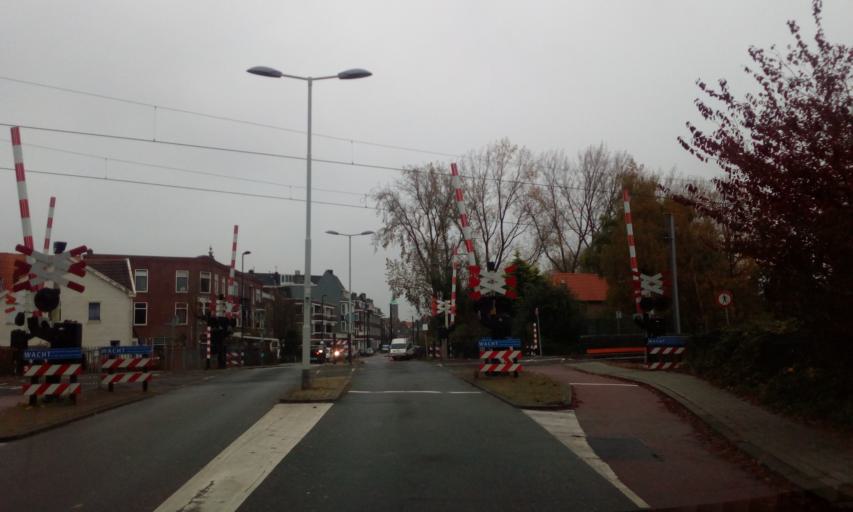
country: NL
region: South Holland
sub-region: Gemeente Rotterdam
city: Rotterdam
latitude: 51.9456
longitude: 4.4658
